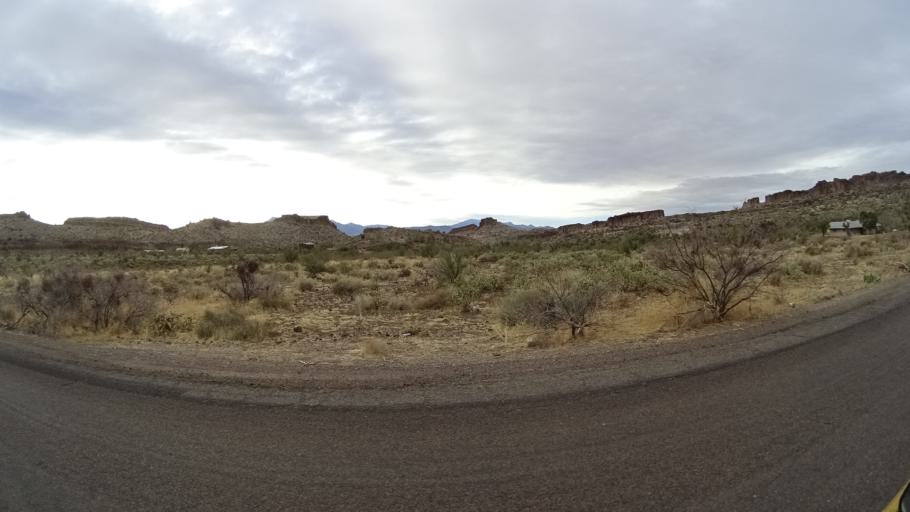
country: US
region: Arizona
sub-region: Mohave County
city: Kingman
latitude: 35.2167
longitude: -114.0735
